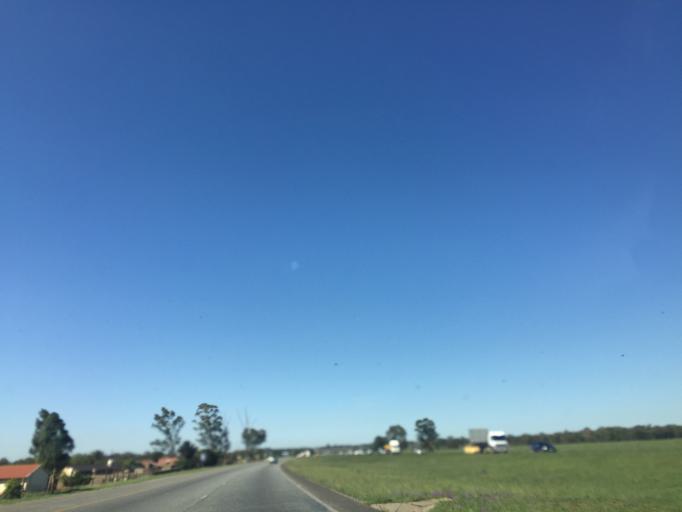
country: ZA
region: Gauteng
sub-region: Sedibeng District Municipality
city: Meyerton
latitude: -26.5263
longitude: 28.0288
